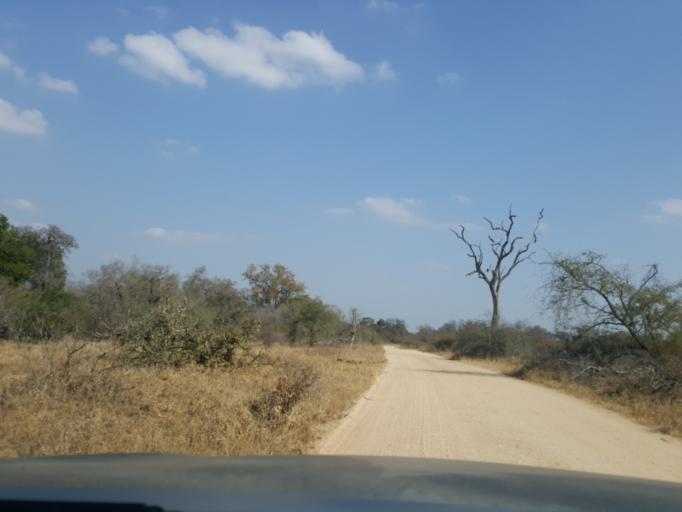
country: ZA
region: Mpumalanga
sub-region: Ehlanzeni District
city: Komatipoort
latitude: -25.2788
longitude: 31.7767
